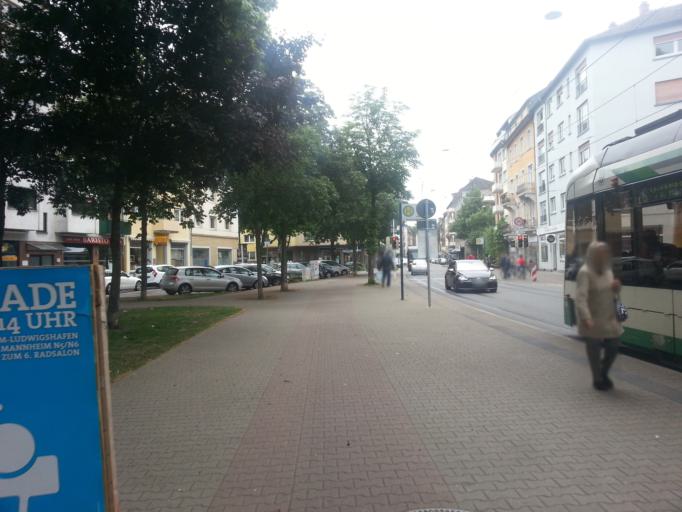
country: DE
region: Baden-Wuerttemberg
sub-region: Karlsruhe Region
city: Mannheim
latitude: 49.4810
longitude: 8.4771
